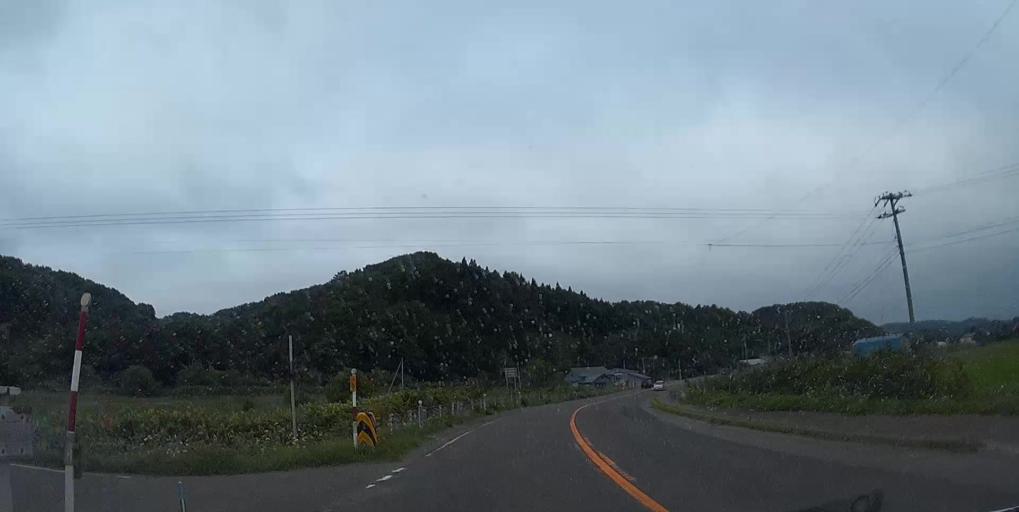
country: JP
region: Hokkaido
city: Iwanai
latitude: 42.4293
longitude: 139.9151
